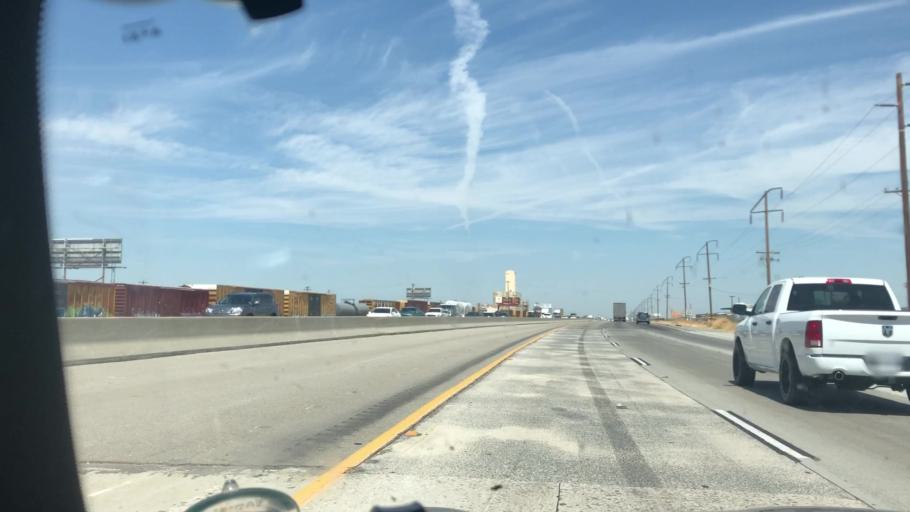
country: US
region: California
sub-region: Kern County
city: Greenacres
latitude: 35.4462
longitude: -119.0934
